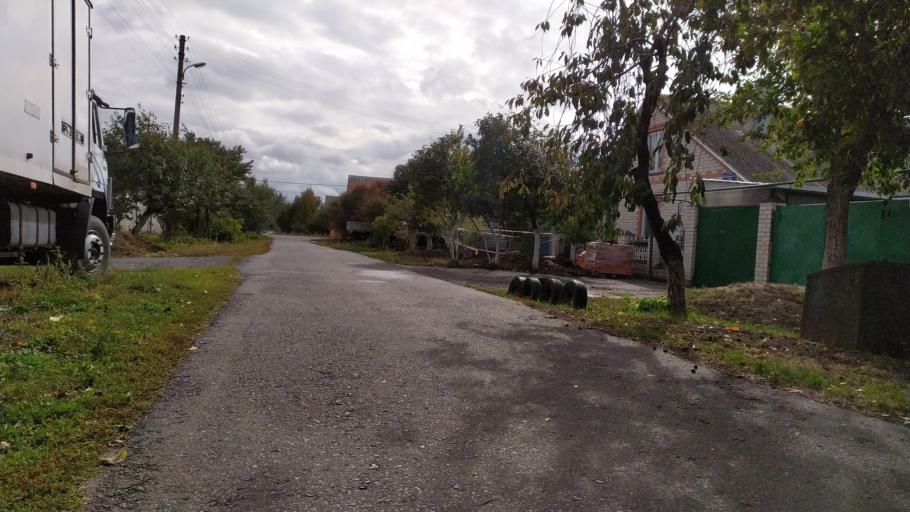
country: RU
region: Kursk
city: Kursk
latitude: 51.6447
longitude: 36.1530
